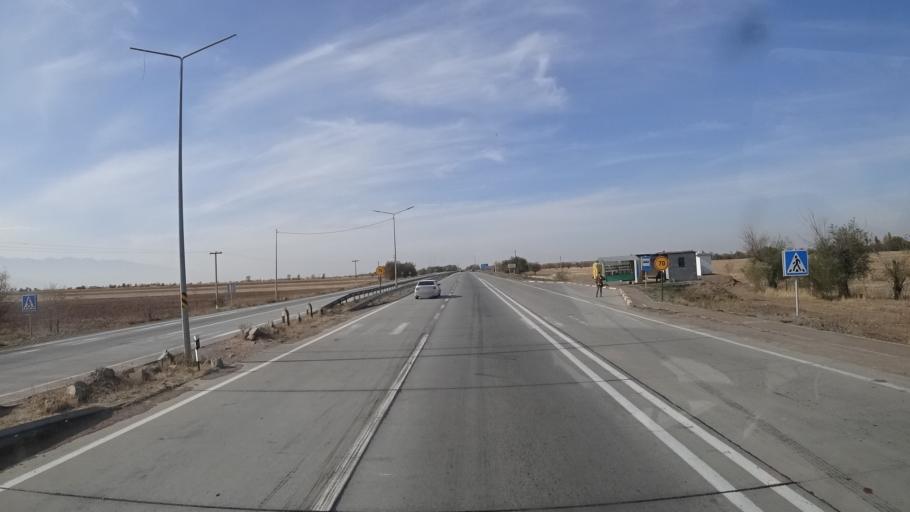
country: KZ
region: Zhambyl
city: Lugovoy
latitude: 42.9061
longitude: 72.9109
